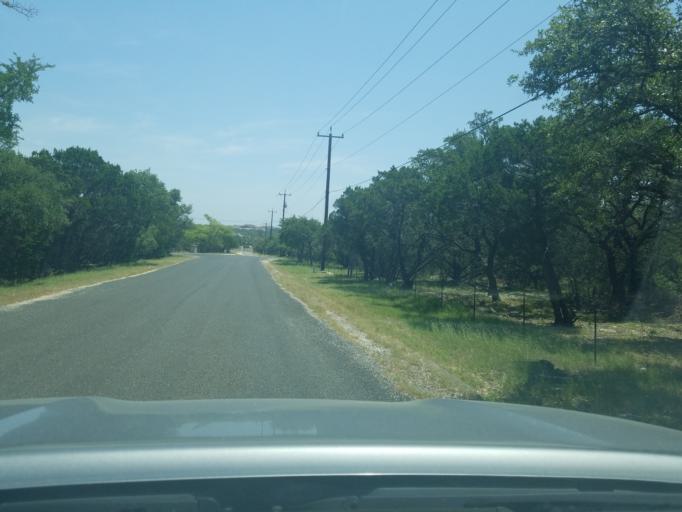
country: US
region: Texas
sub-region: Bexar County
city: Timberwood Park
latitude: 29.6775
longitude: -98.4939
